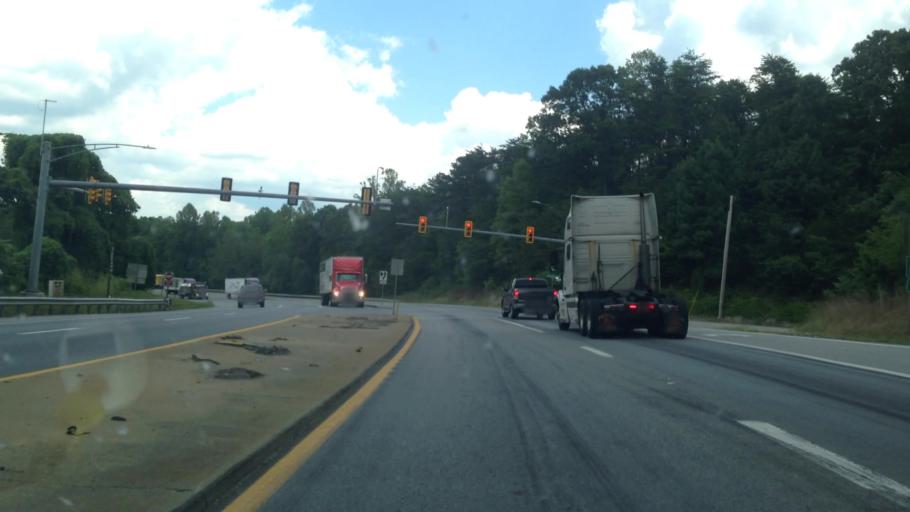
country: US
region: Virginia
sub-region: Henry County
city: Chatmoss
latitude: 36.5786
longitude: -79.8635
